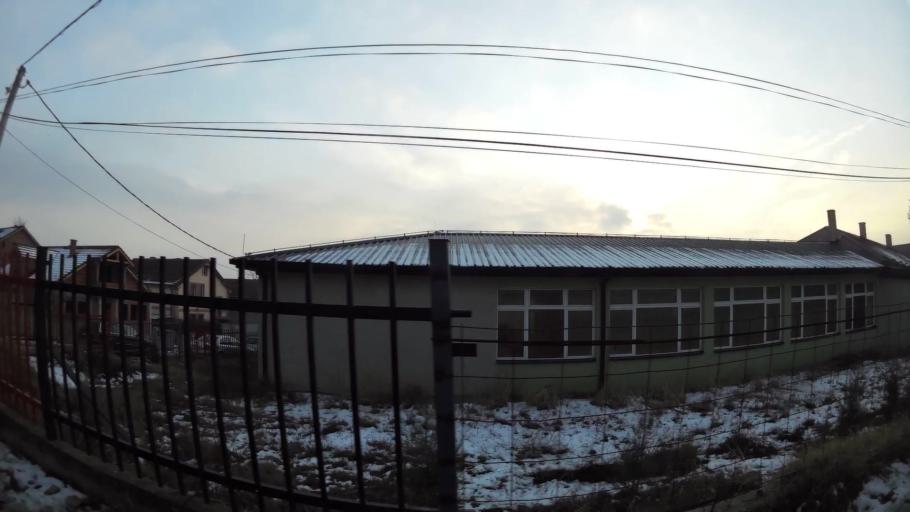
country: MK
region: Aracinovo
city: Arachinovo
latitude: 42.0241
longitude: 21.5610
